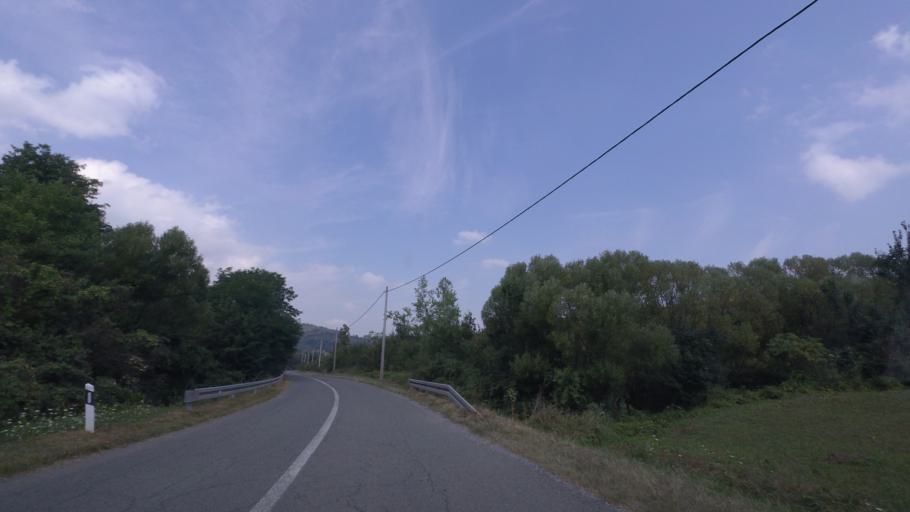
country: BA
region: Federation of Bosnia and Herzegovina
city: Zboriste
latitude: 45.1803
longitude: 16.1344
